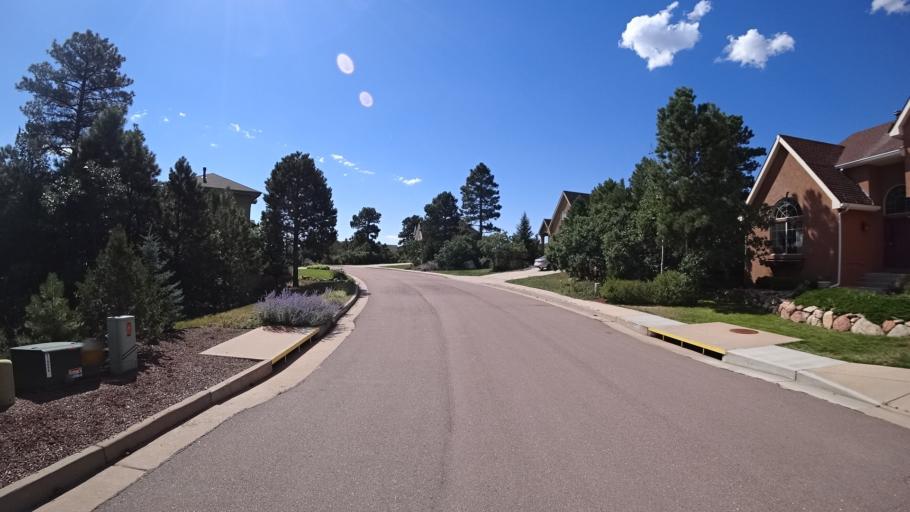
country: US
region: Colorado
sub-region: El Paso County
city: Fort Carson
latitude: 38.7431
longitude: -104.8393
